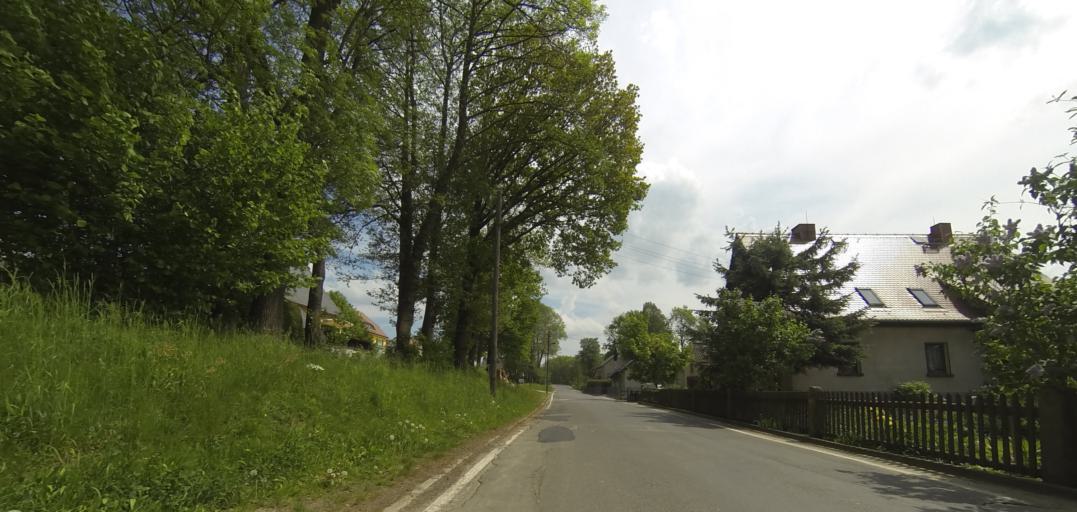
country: DE
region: Saxony
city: Grossrohrsdorf
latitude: 51.0991
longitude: 14.0454
